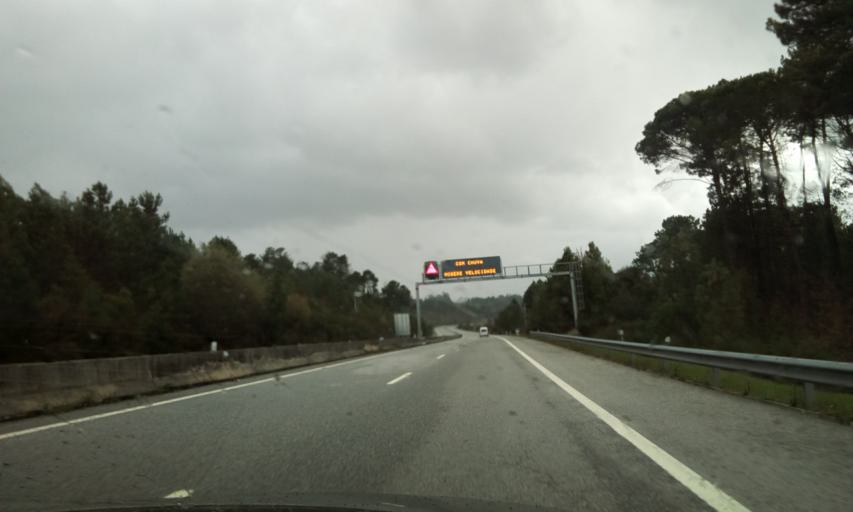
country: PT
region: Viseu
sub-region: Viseu
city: Rio de Loba
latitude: 40.6366
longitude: -7.8807
